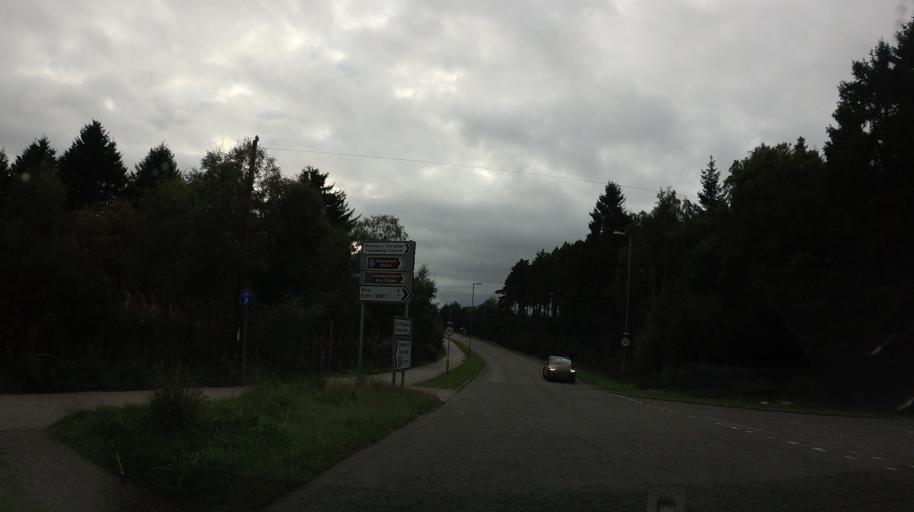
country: GB
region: Scotland
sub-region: Aberdeenshire
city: Banchory
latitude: 57.0623
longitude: -2.4672
